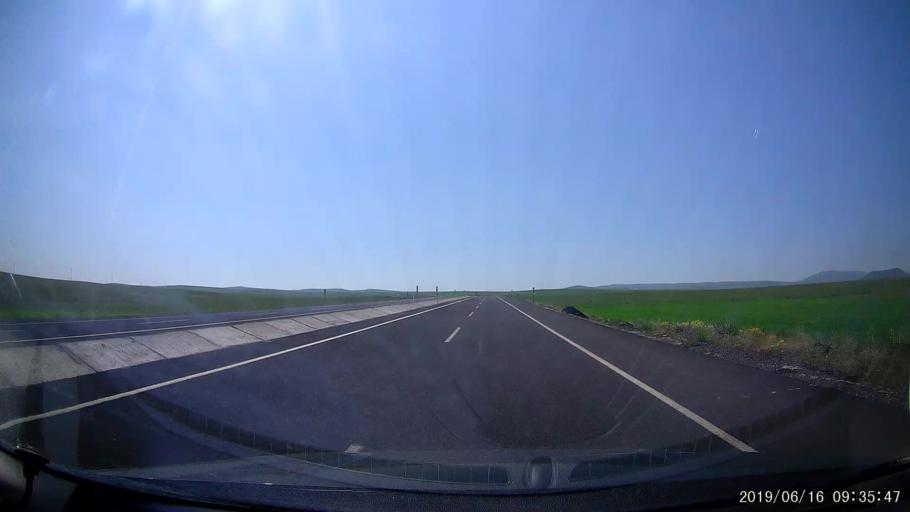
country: TR
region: Kars
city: Kars
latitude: 40.5663
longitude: 43.1619
